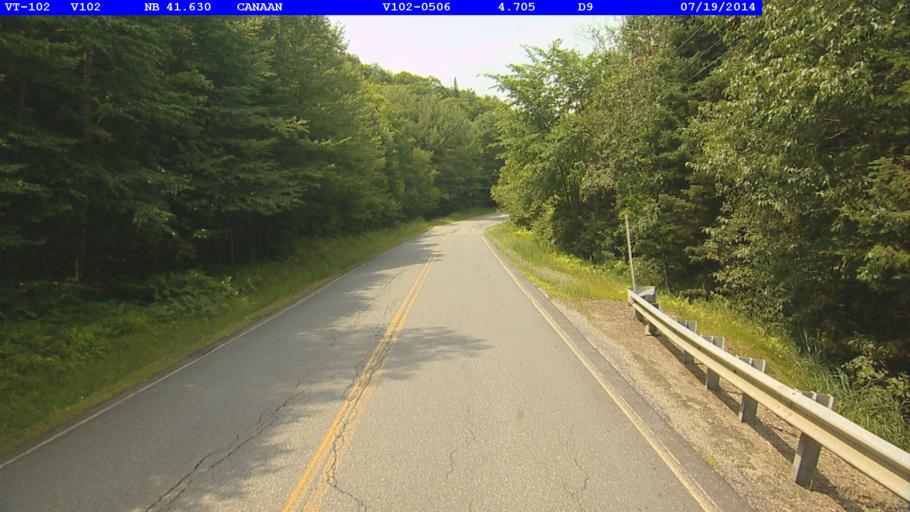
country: US
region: New Hampshire
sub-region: Coos County
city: Colebrook
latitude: 44.9713
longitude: -71.5289
